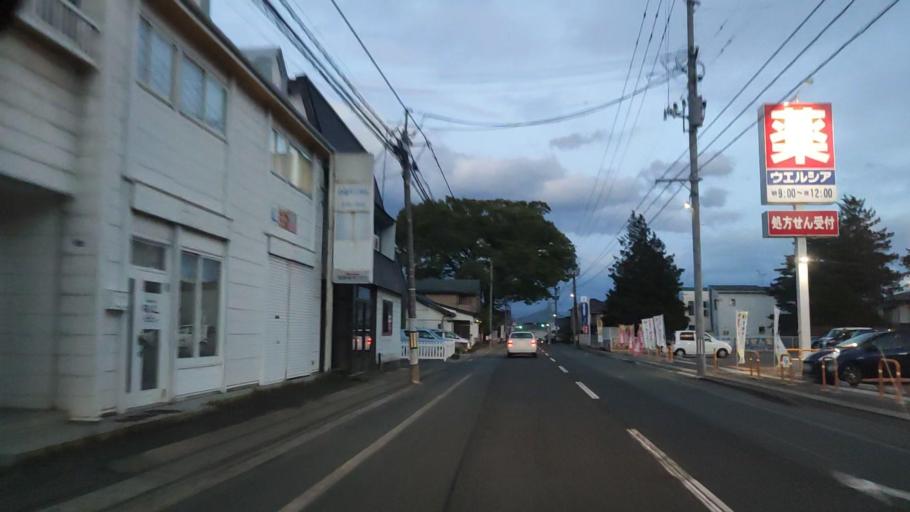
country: JP
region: Iwate
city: Morioka-shi
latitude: 39.7173
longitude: 141.1234
